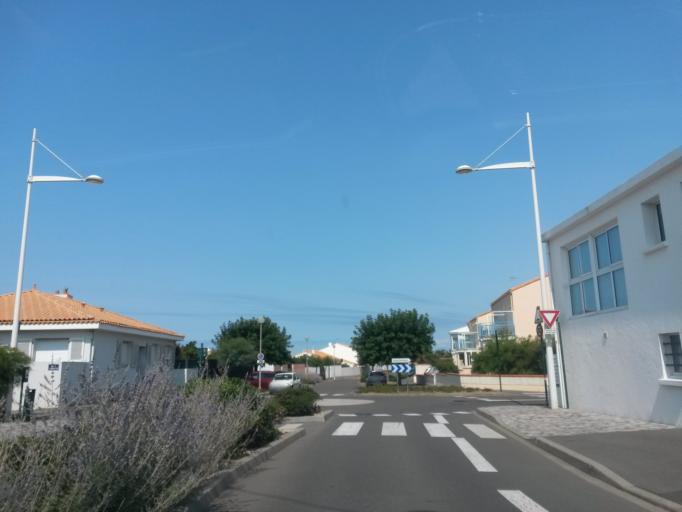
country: FR
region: Pays de la Loire
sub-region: Departement de la Vendee
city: Les Sables-d'Olonne
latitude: 46.4951
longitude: -1.8123
